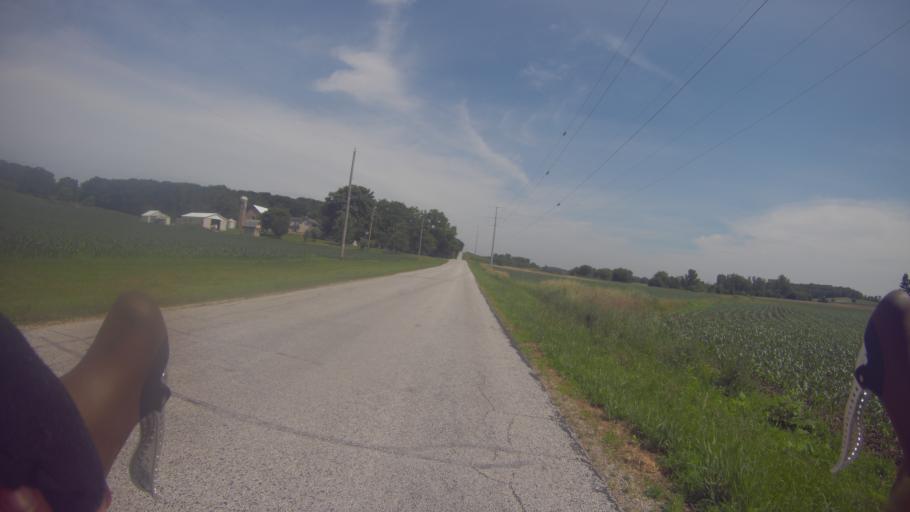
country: US
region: Wisconsin
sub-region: Dane County
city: Deerfield
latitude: 43.0459
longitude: -89.0417
